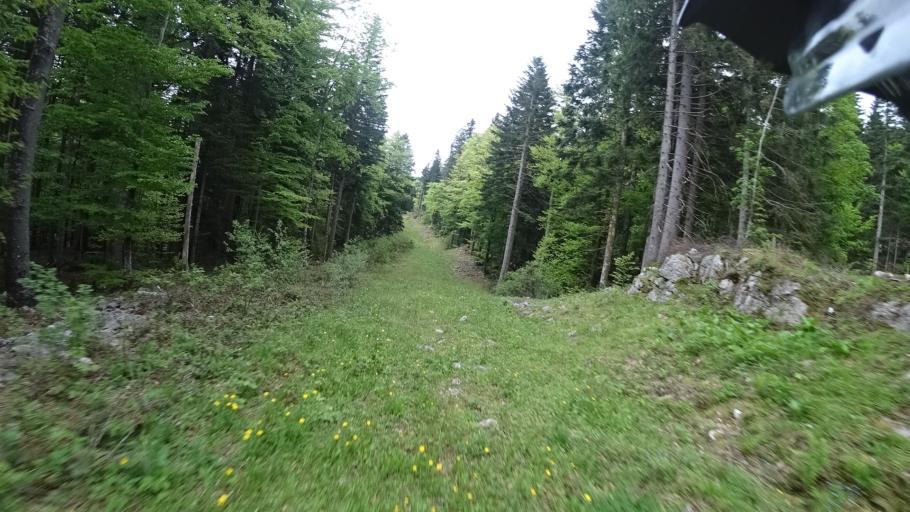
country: HR
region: Karlovacka
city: Plaski
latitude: 44.9585
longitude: 15.4128
